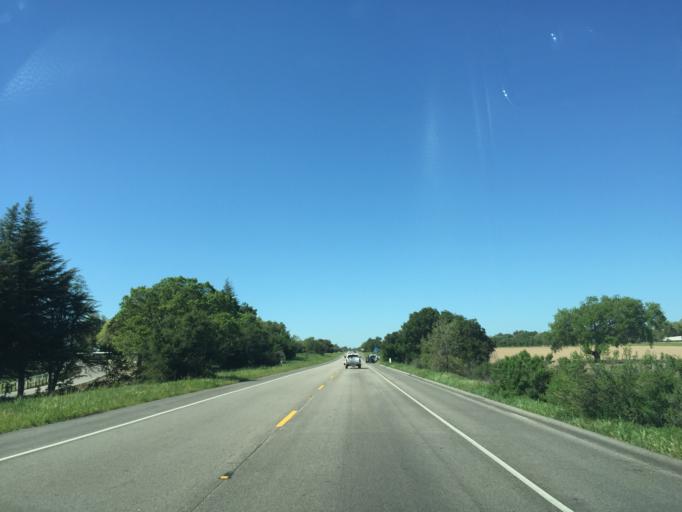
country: US
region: California
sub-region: Santa Barbara County
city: Santa Ynez
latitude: 34.6442
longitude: -120.0899
